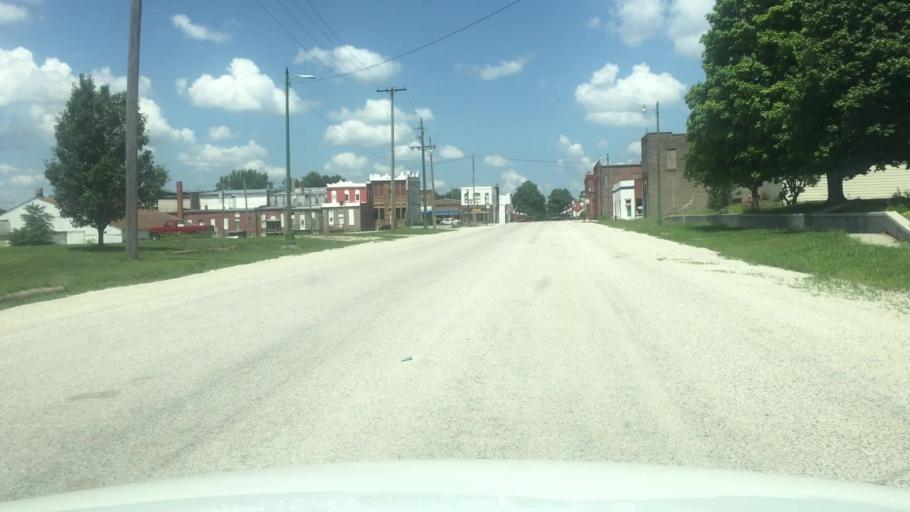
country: US
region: Kansas
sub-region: Brown County
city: Horton
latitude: 39.6580
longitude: -95.5274
